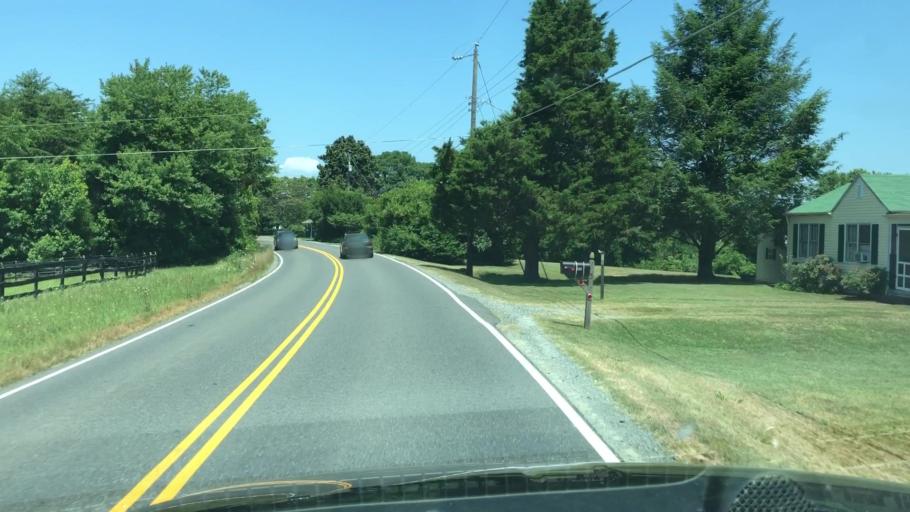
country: US
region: Virginia
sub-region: Stafford County
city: Falmouth
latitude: 38.4158
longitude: -77.5695
